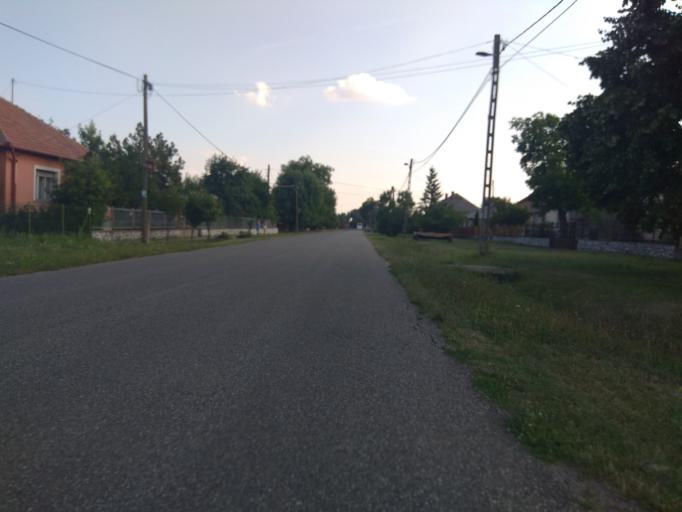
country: HU
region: Borsod-Abauj-Zemplen
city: Mezokeresztes
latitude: 47.8662
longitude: 20.6791
